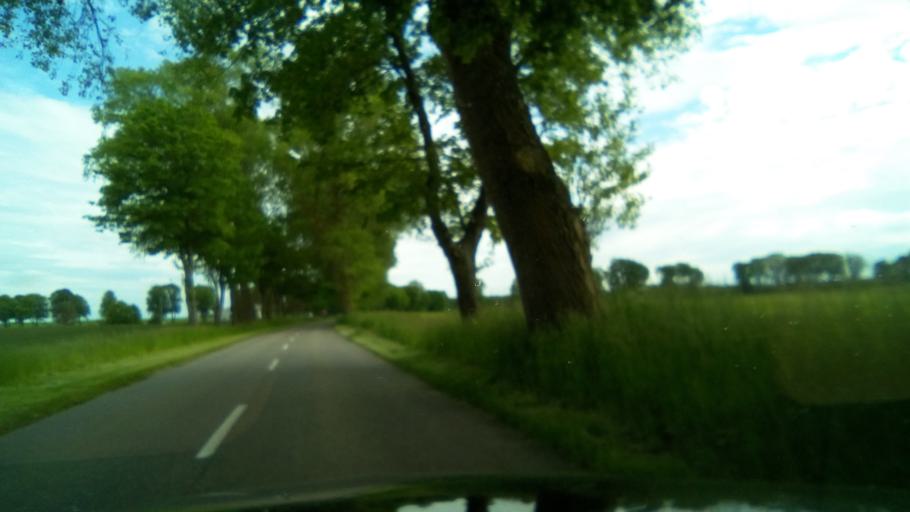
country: PL
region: Pomeranian Voivodeship
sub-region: Powiat pucki
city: Krokowa
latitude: 54.7904
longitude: 18.1178
